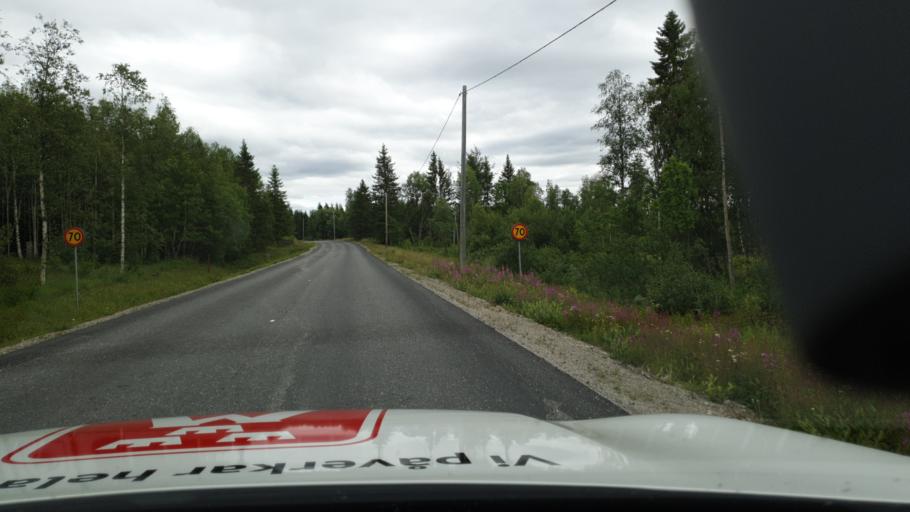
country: SE
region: Vaesterbotten
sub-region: Lycksele Kommun
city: Soderfors
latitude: 64.6449
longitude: 17.8605
